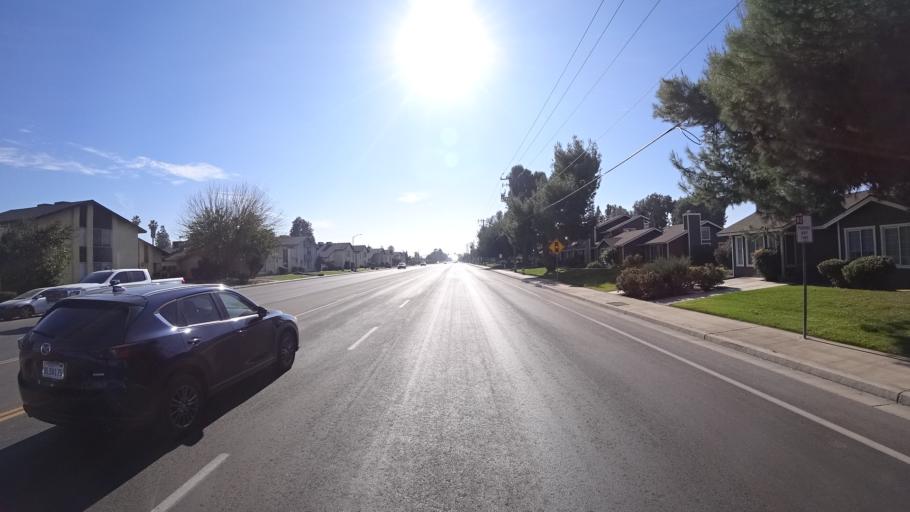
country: US
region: California
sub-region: Kern County
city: Greenacres
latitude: 35.3322
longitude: -119.0745
